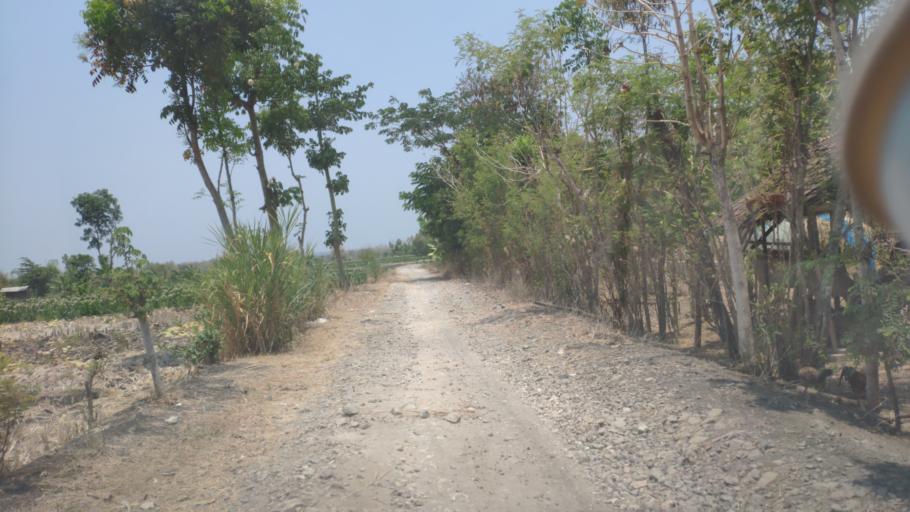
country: ID
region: Central Java
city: Temulus
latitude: -7.2254
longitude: 111.4255
